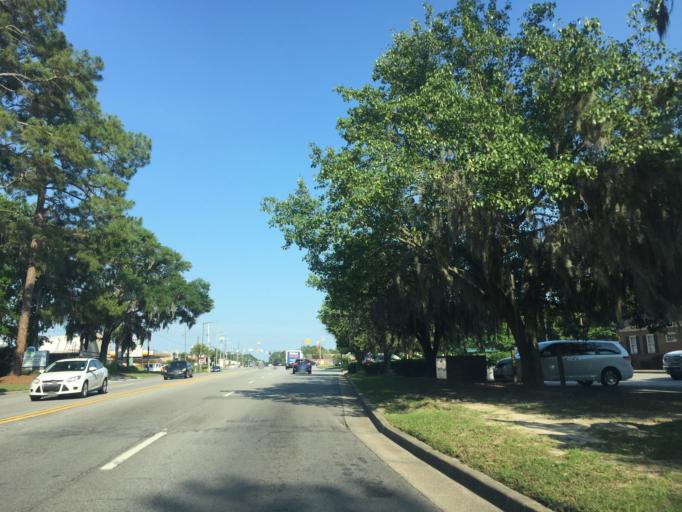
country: US
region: Georgia
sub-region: Chatham County
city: Isle of Hope
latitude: 32.0072
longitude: -81.1031
